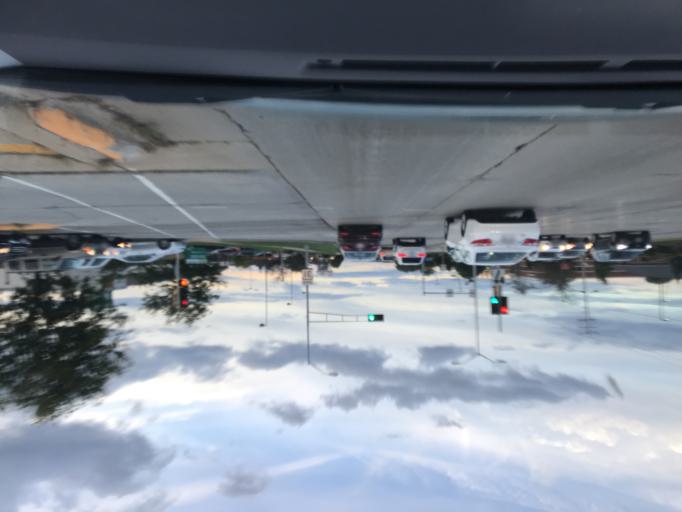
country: US
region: Wisconsin
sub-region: Kenosha County
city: Pleasant Prairie
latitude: 42.5743
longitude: -87.8859
